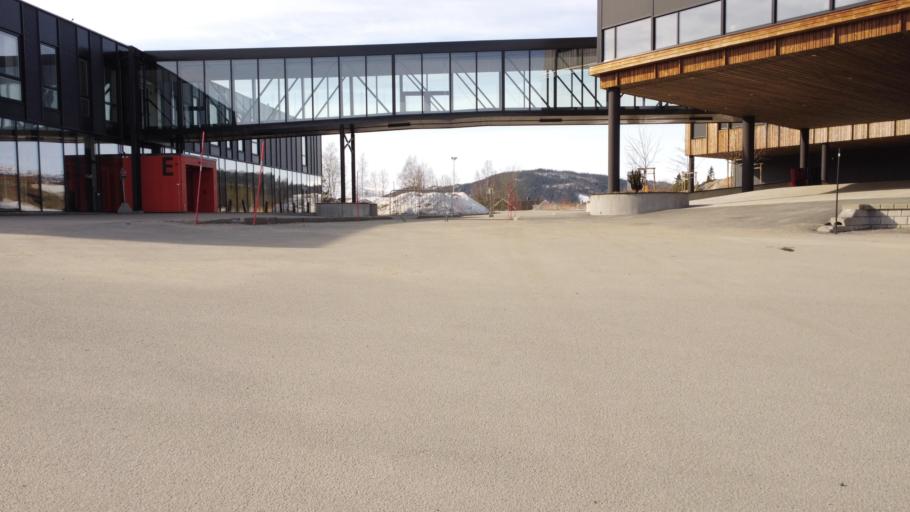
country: NO
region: Nordland
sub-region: Rana
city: Mo i Rana
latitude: 66.3301
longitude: 14.1577
